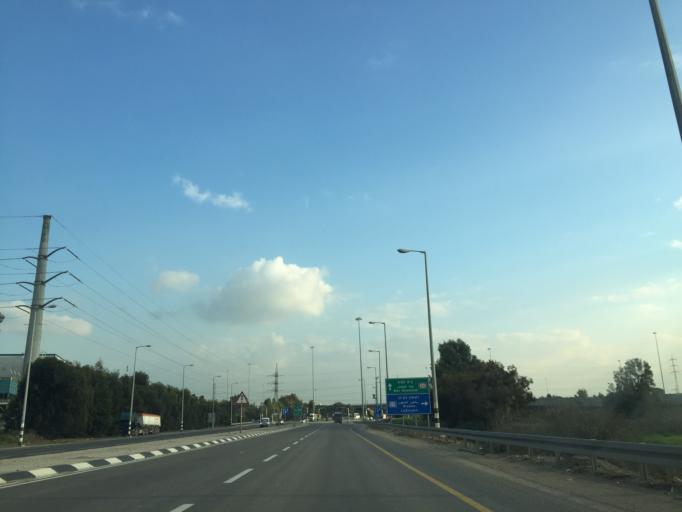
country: IL
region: Central District
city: Ramla
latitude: 31.9147
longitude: 34.8888
